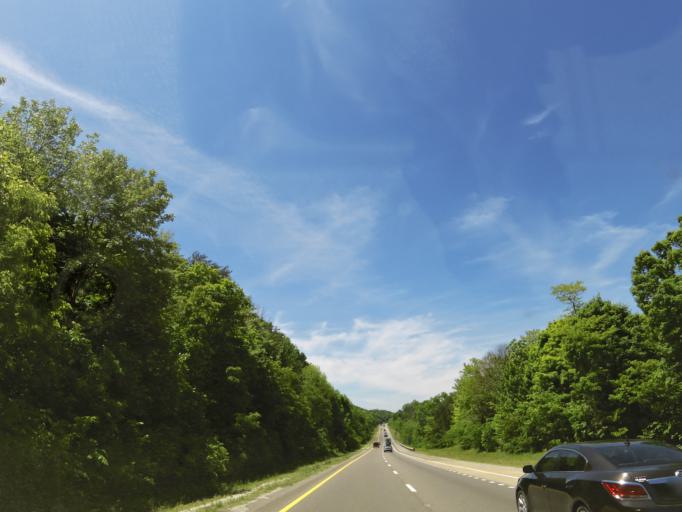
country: US
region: Tennessee
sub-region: Campbell County
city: Jellico
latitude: 36.5275
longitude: -84.1743
